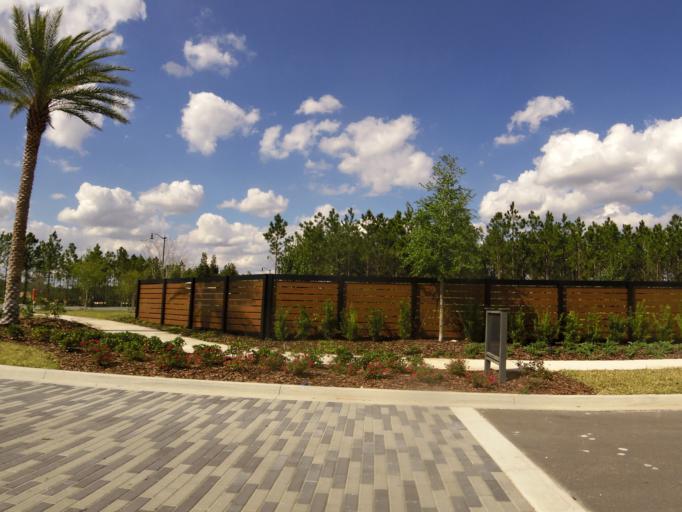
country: US
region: Florida
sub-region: Saint Johns County
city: Palm Valley
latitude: 30.1968
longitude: -81.5075
